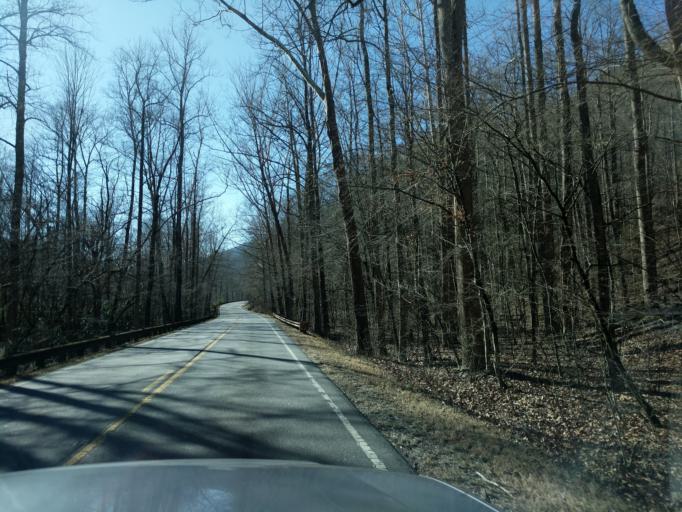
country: US
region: North Carolina
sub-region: Graham County
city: Robbinsville
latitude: 35.2826
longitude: -83.6738
